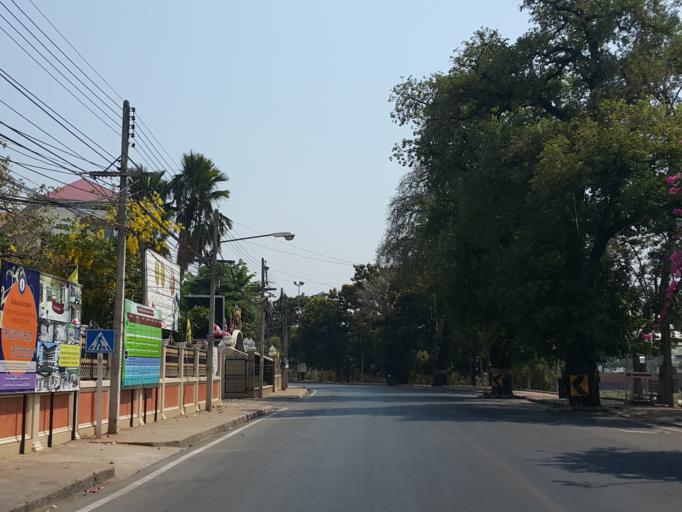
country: TH
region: Phitsanulok
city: Phitsanulok
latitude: 16.8208
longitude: 100.2597
